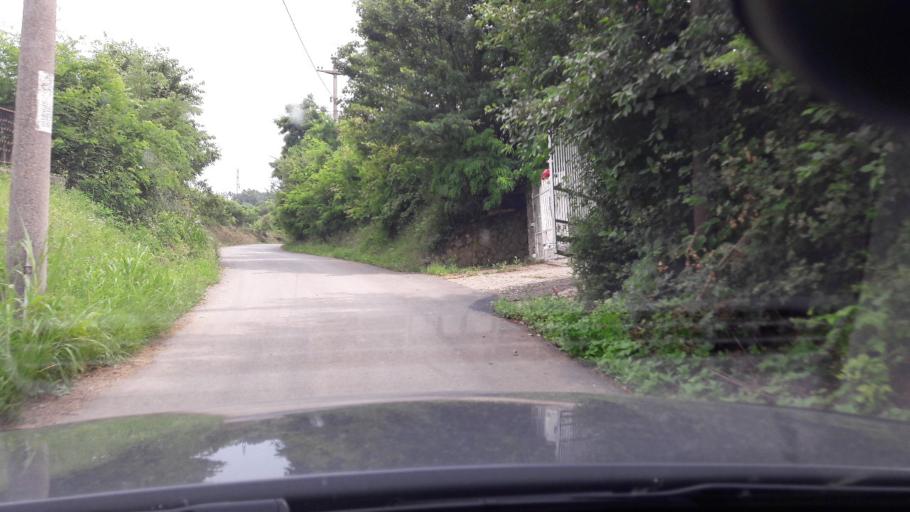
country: RS
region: Central Serbia
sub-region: Belgrade
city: Grocka
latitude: 44.6432
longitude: 20.6066
